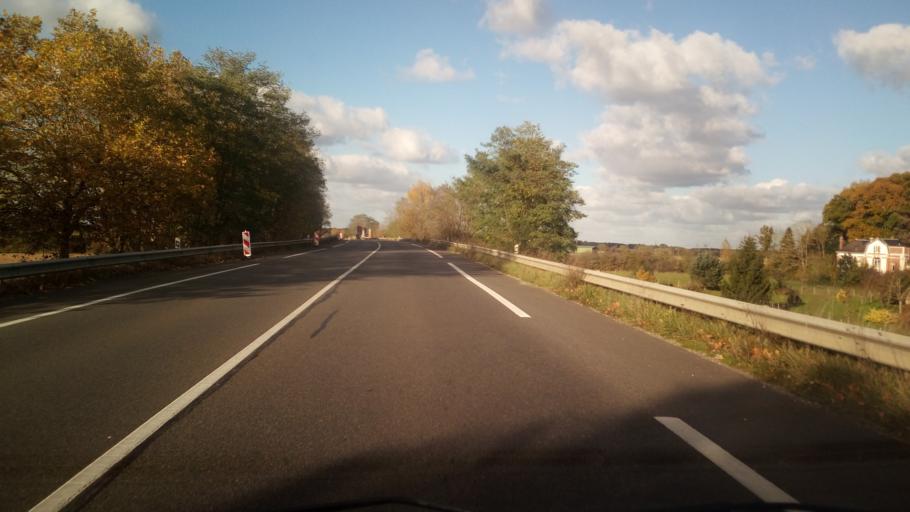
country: FR
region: Centre
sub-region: Departement du Loiret
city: Gien
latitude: 47.6896
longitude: 2.6508
